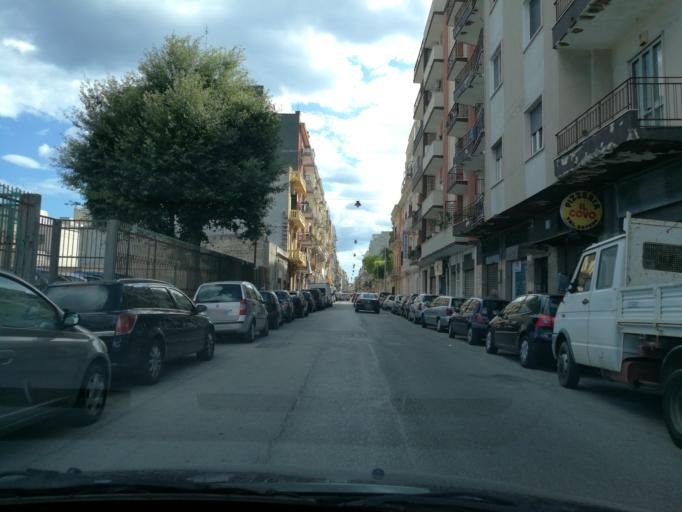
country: IT
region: Apulia
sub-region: Provincia di Bari
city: Bari
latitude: 41.1271
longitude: 16.8532
